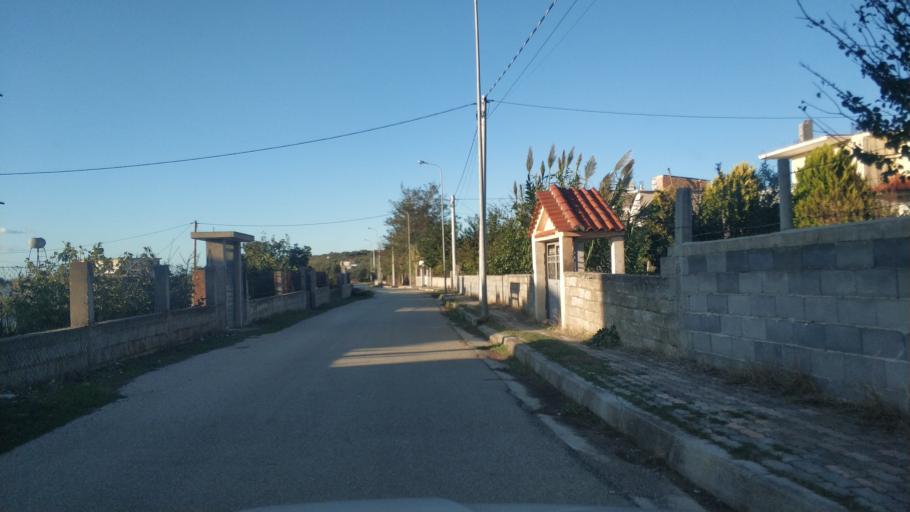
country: AL
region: Vlore
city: Vlore
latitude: 40.5089
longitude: 19.4104
